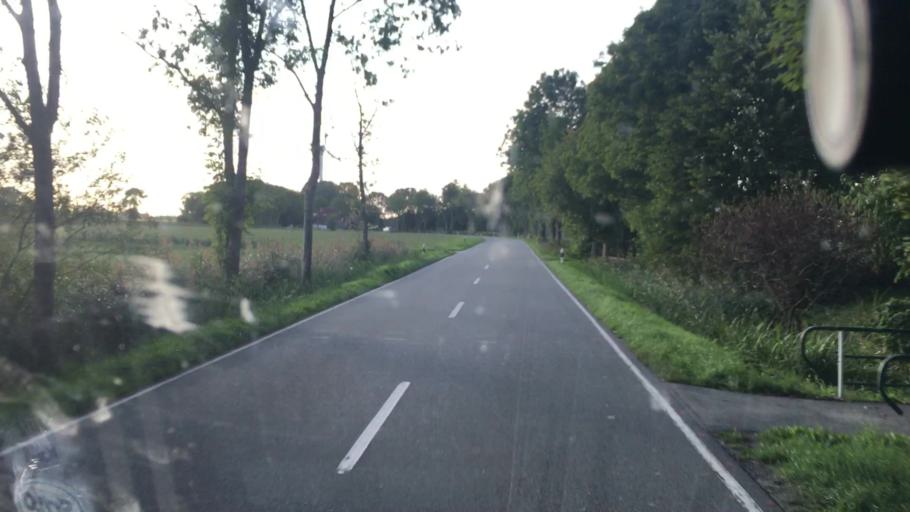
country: DE
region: Lower Saxony
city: Wittmund
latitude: 53.6423
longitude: 7.8146
